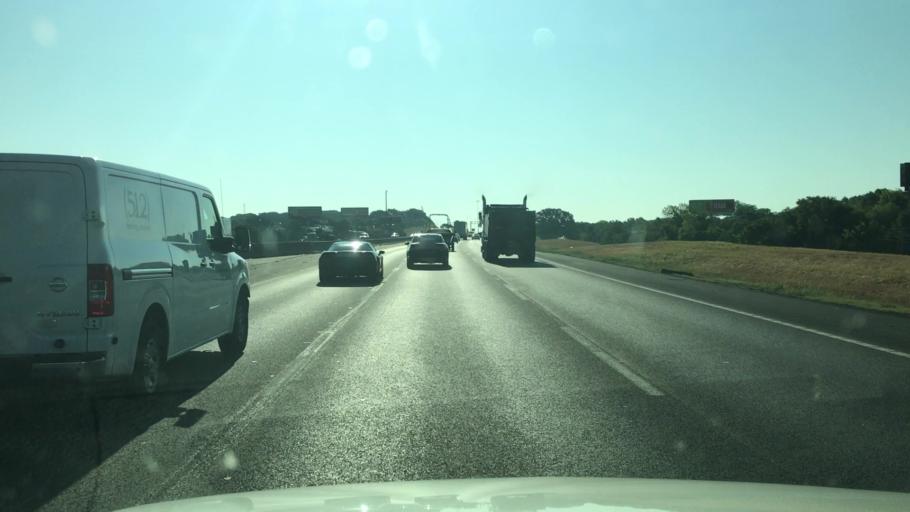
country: US
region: Texas
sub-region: Tarrant County
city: Haltom City
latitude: 32.7606
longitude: -97.2379
